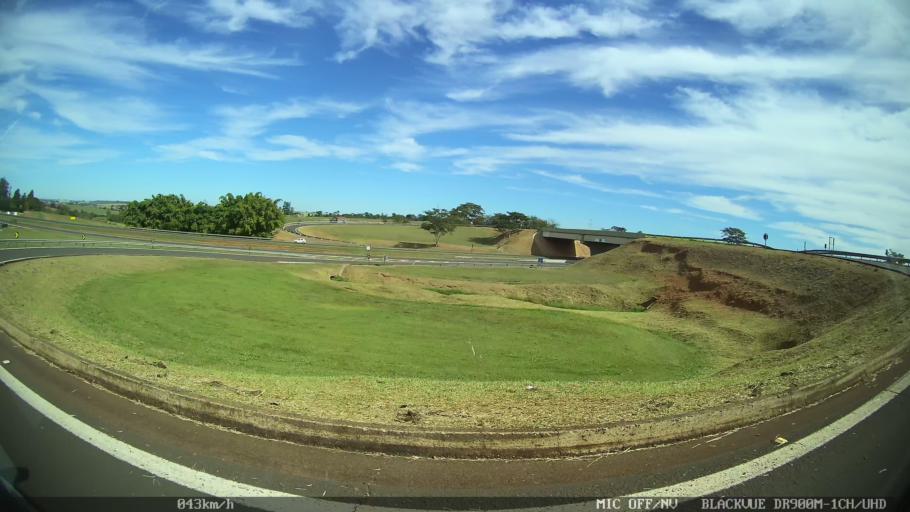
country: BR
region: Sao Paulo
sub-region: Taquaritinga
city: Taquaritinga
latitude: -21.5154
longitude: -48.5398
